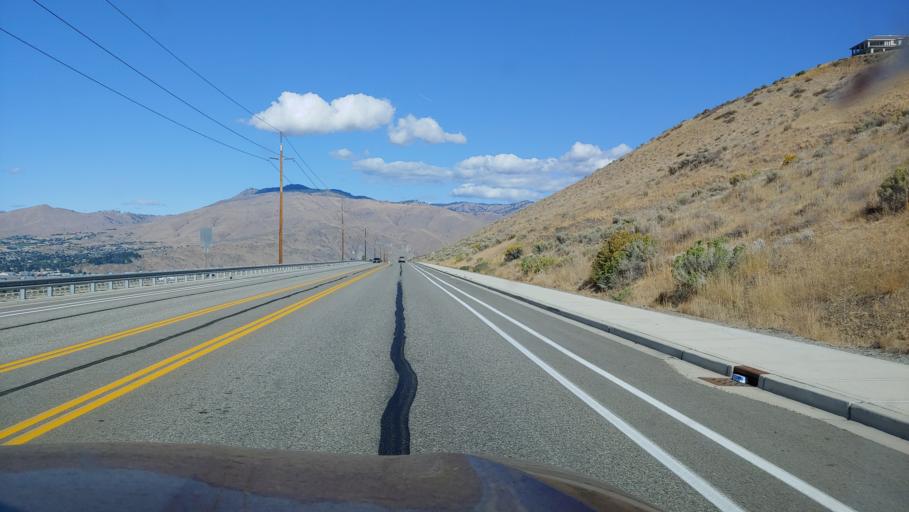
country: US
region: Washington
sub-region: Douglas County
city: East Wenatchee Bench
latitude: 47.4441
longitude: -120.2845
